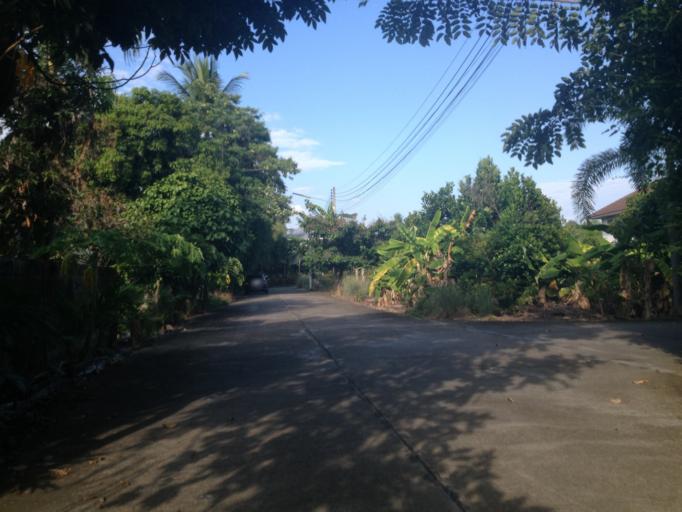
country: TH
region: Chiang Mai
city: Hang Dong
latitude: 18.7114
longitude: 98.9252
